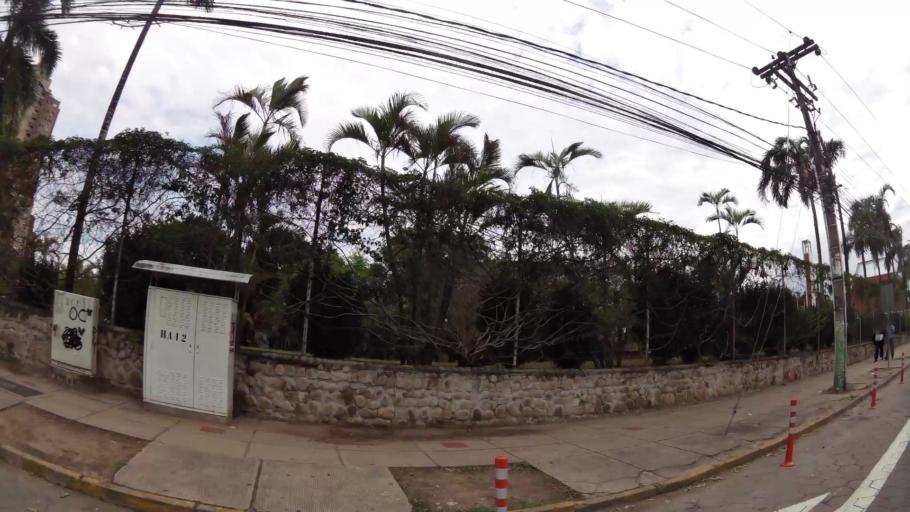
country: BO
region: Santa Cruz
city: Santa Cruz de la Sierra
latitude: -17.7705
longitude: -63.1850
